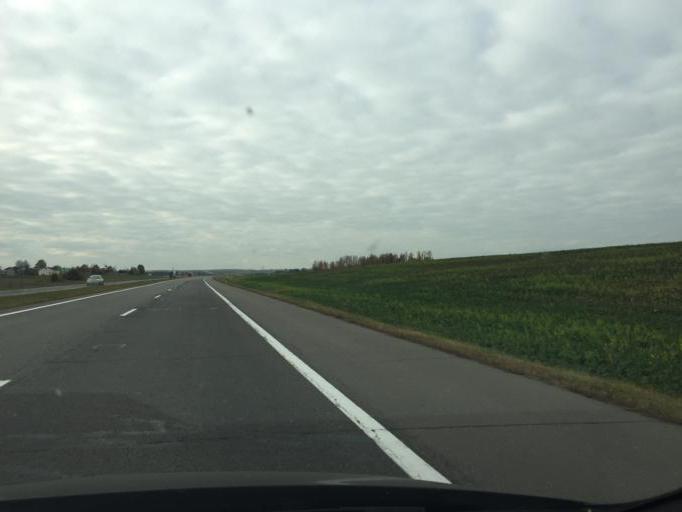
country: BY
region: Minsk
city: Stan'kava
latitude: 53.6786
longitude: 27.2707
